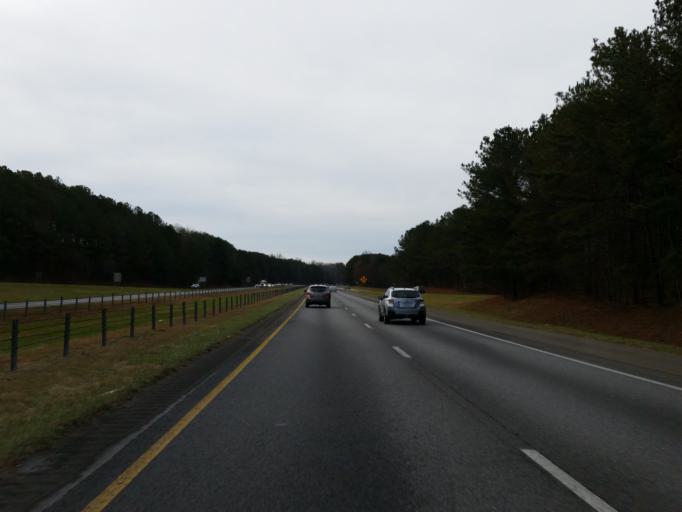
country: US
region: Georgia
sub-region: Cherokee County
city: Holly Springs
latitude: 34.1874
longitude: -84.5063
